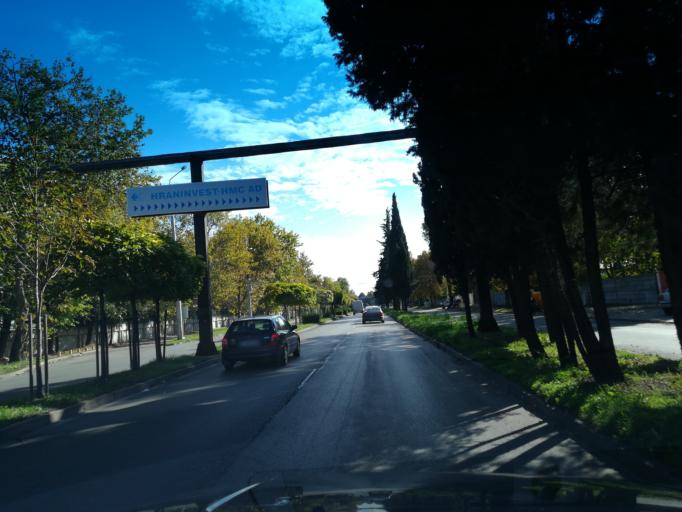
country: BG
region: Stara Zagora
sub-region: Obshtina Stara Zagora
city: Stara Zagora
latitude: 42.4124
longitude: 25.6389
